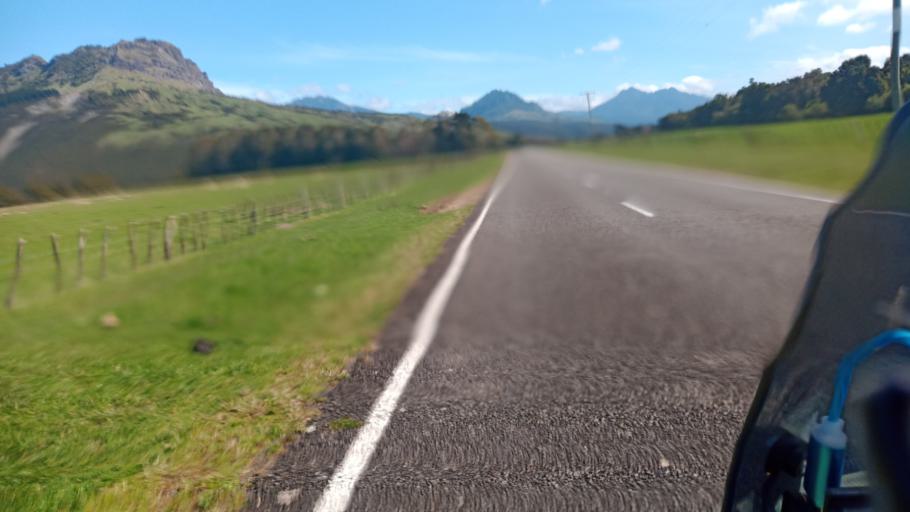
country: NZ
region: Gisborne
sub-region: Gisborne District
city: Gisborne
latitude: -37.8651
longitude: 178.2180
